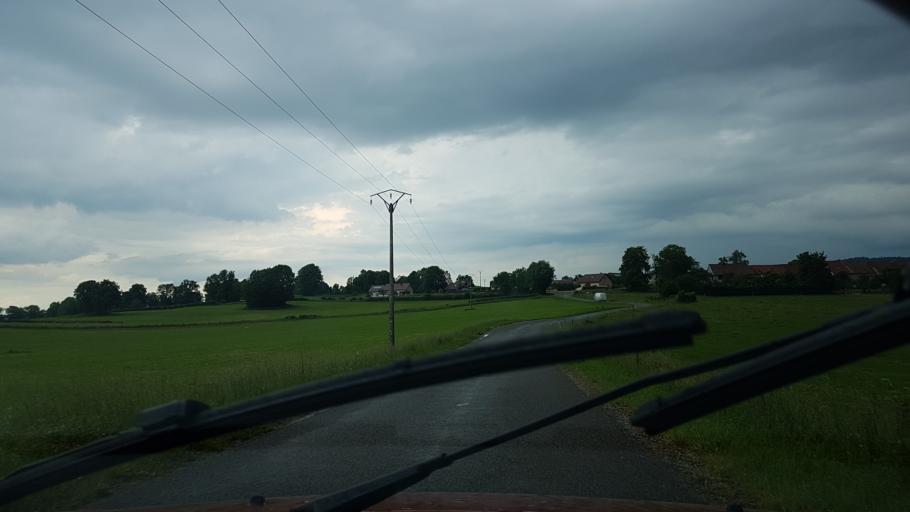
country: FR
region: Franche-Comte
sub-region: Departement du Jura
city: Clairvaux-les-Lacs
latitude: 46.5395
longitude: 5.7444
